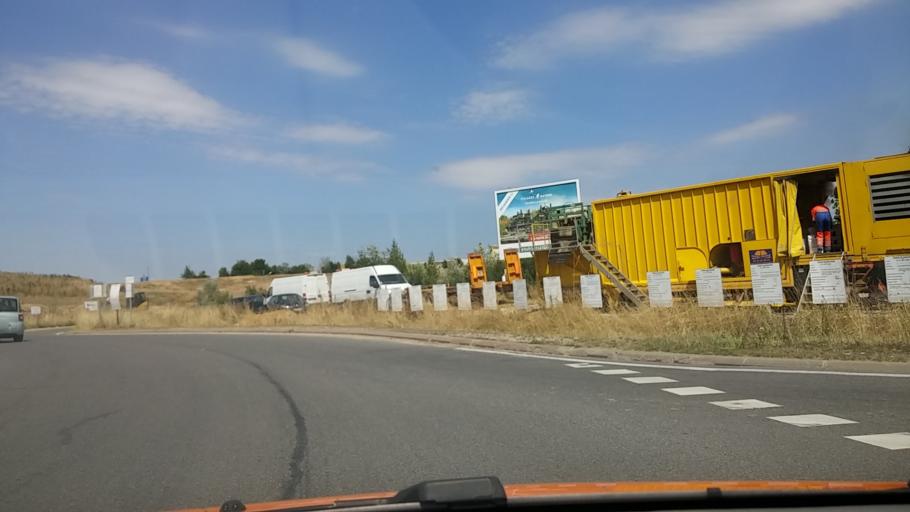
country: FR
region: Ile-de-France
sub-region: Departement de Seine-et-Marne
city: Serris
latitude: 48.8315
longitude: 2.7996
